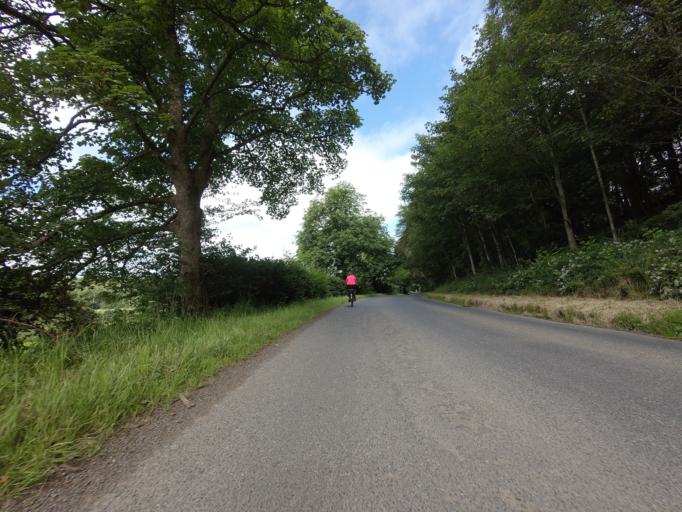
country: GB
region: Scotland
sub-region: Aberdeenshire
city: Turriff
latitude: 57.5503
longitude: -2.4855
